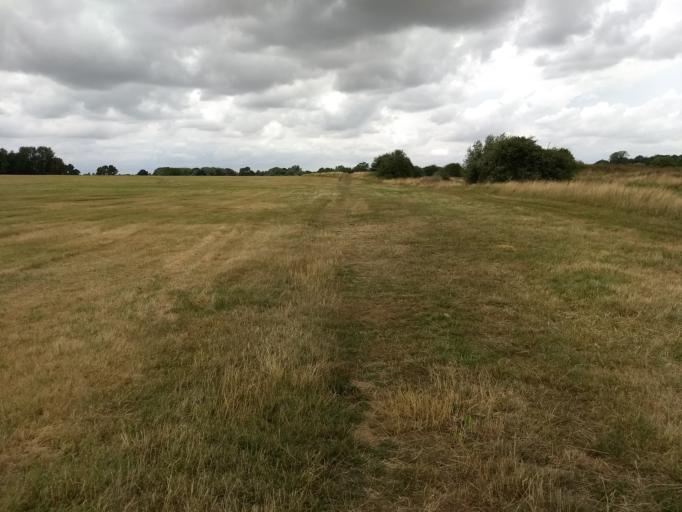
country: GB
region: England
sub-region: Milton Keynes
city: Newport Pagnell
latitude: 52.0891
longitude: -0.7287
